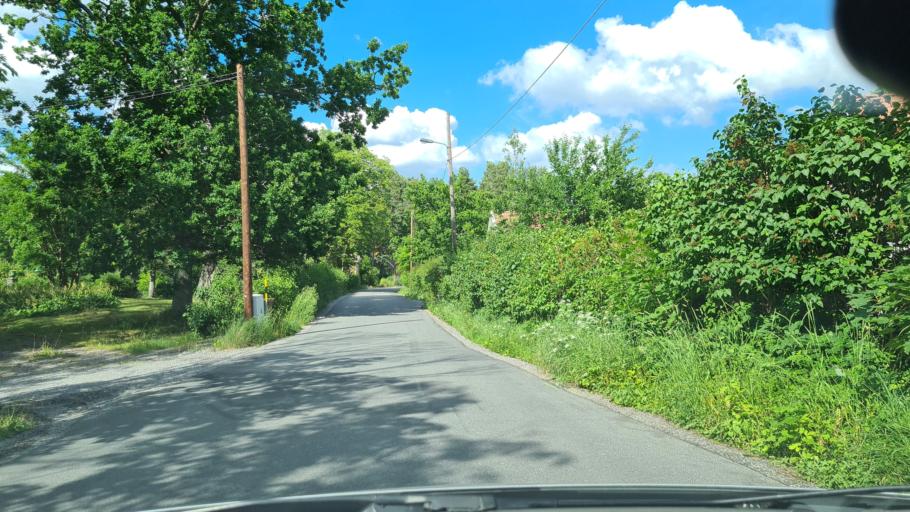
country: SE
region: Stockholm
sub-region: Vaxholms Kommun
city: Vaxholm
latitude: 59.4090
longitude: 18.3701
